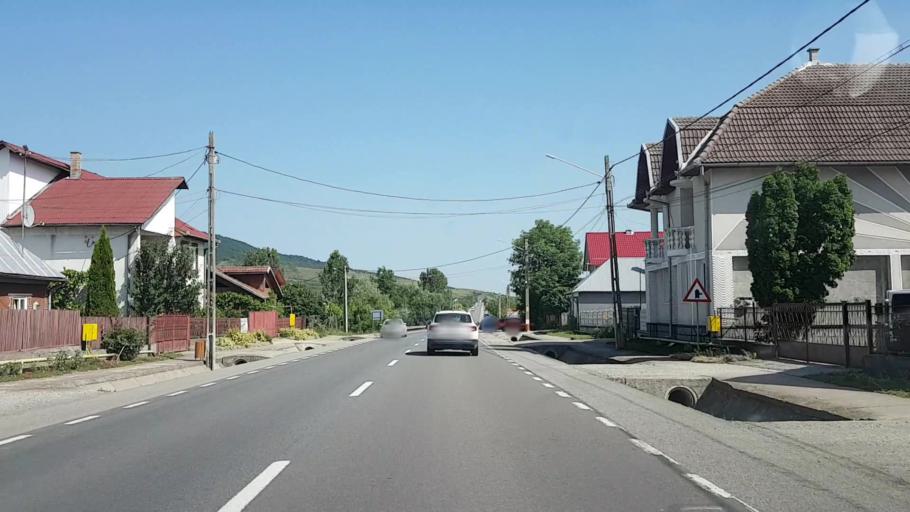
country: RO
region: Bistrita-Nasaud
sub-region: Comuna Sieu-Magherus
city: Sieu-Magherus
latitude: 47.0881
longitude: 24.3793
